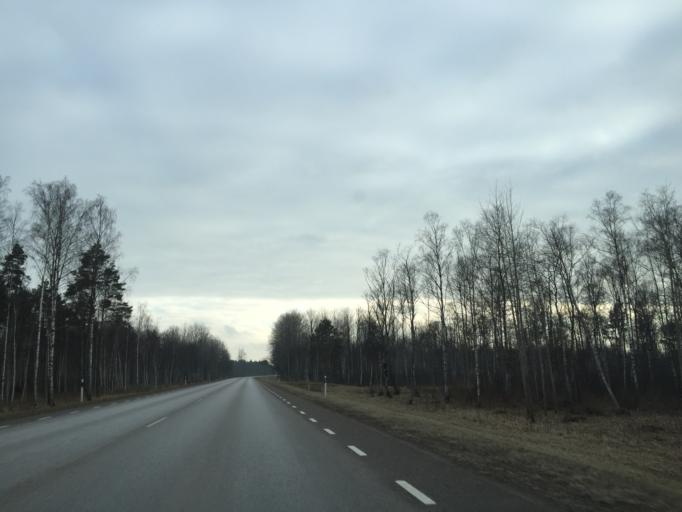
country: EE
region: Saare
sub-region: Orissaare vald
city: Orissaare
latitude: 58.4580
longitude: 22.8089
